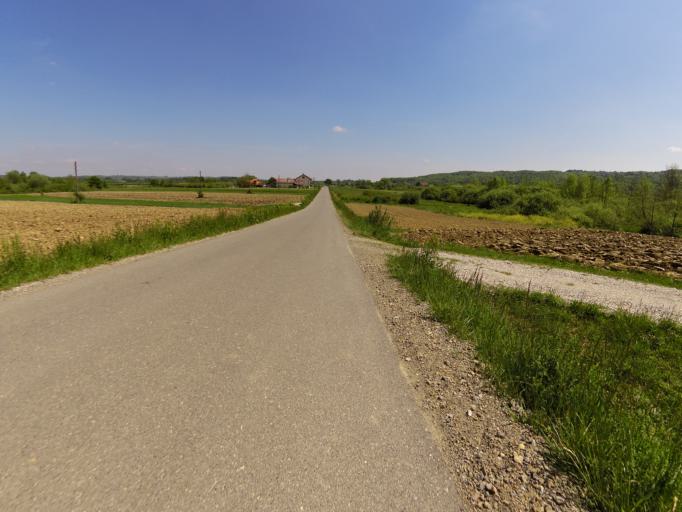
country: HR
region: Karlovacka
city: Ozalj
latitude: 45.5621
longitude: 15.4905
